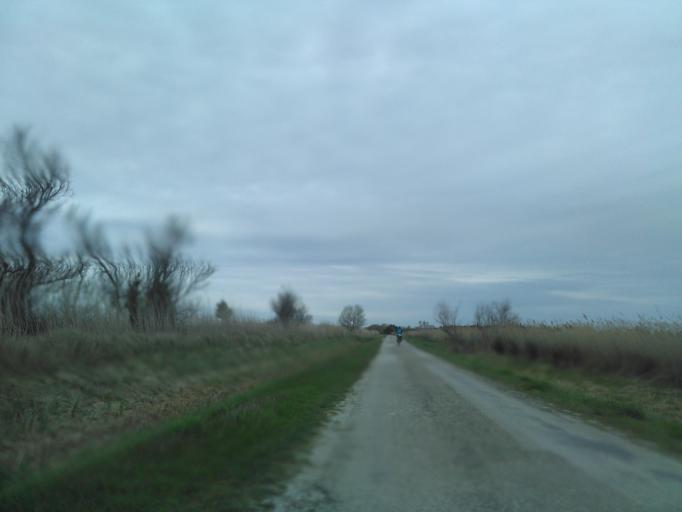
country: FR
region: Provence-Alpes-Cote d'Azur
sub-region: Departement des Bouches-du-Rhone
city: Arles
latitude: 43.5760
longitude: 4.5442
